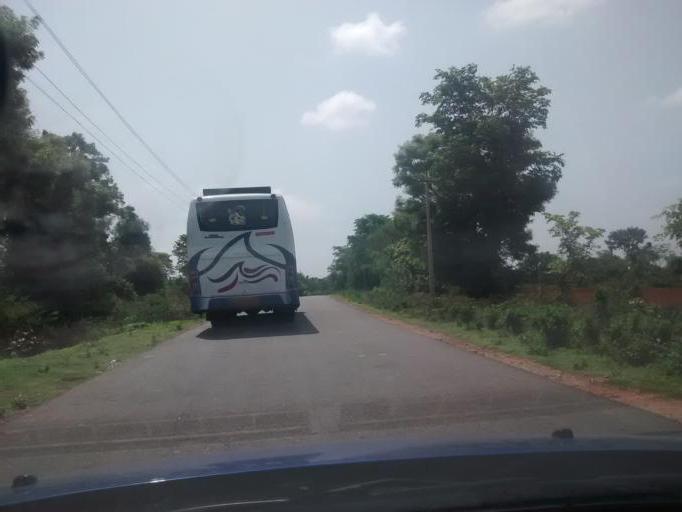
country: IN
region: Karnataka
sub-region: Hassan
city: Konanur
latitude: 12.5819
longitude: 76.1909
